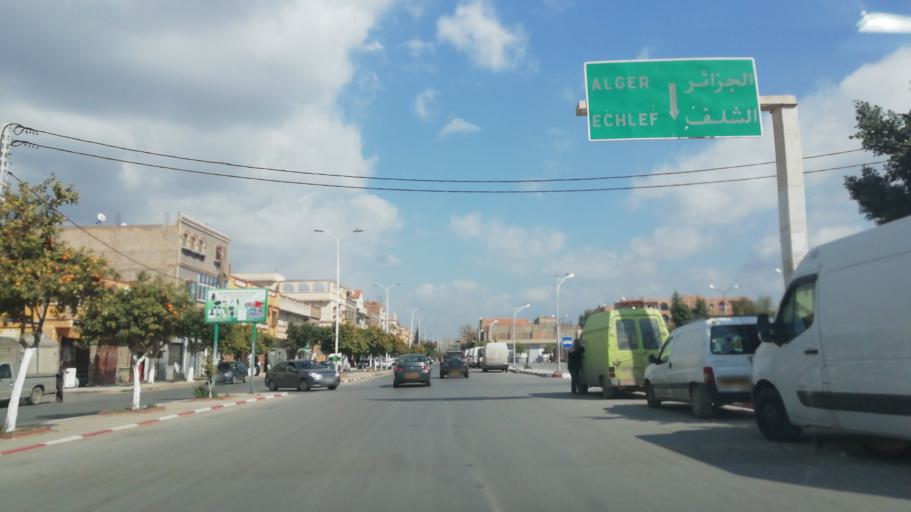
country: DZ
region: Mascara
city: Mascara
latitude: 35.5942
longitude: 0.0728
